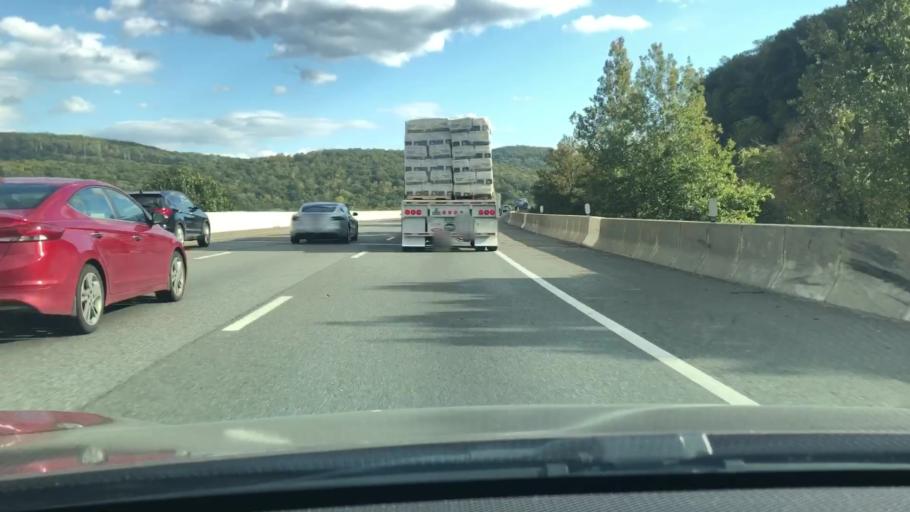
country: US
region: New York
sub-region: Rockland County
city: Sloatsburg
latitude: 41.1403
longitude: -74.1713
